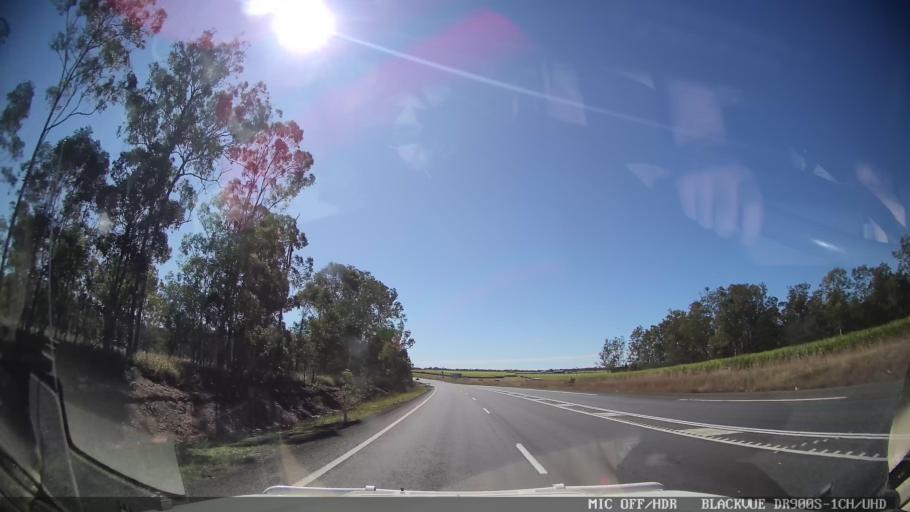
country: AU
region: Queensland
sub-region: Fraser Coast
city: Maryborough
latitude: -25.6467
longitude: 152.6365
